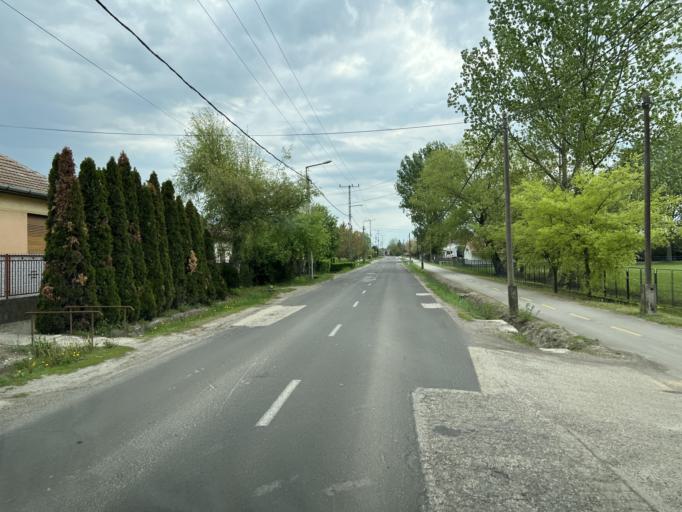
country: HU
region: Pest
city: Farmos
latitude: 47.3653
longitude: 19.8543
